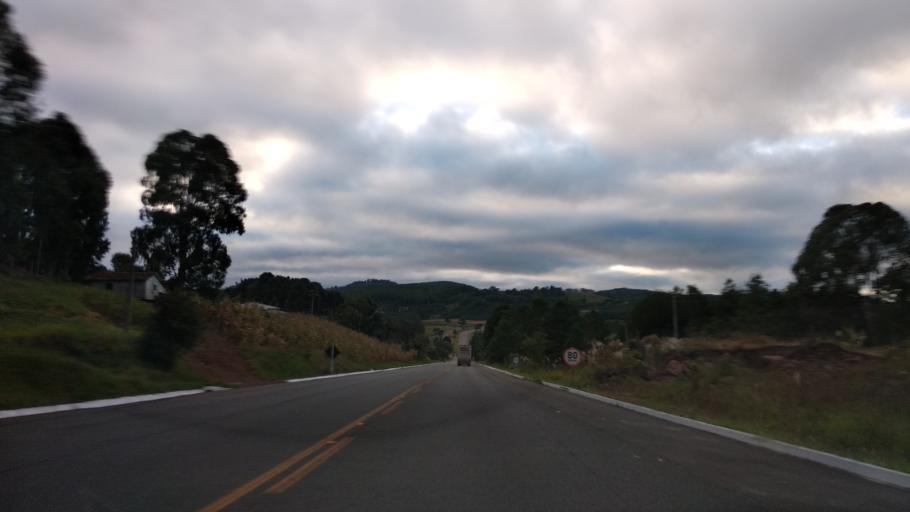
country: BR
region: Santa Catarina
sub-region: Campos Novos
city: Campos Novos
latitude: -27.4952
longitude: -50.9638
